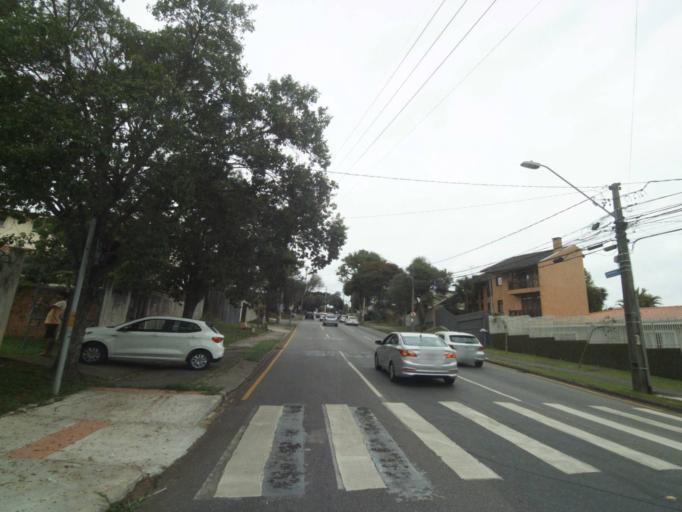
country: BR
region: Parana
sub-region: Curitiba
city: Curitiba
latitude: -25.3992
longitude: -49.2738
